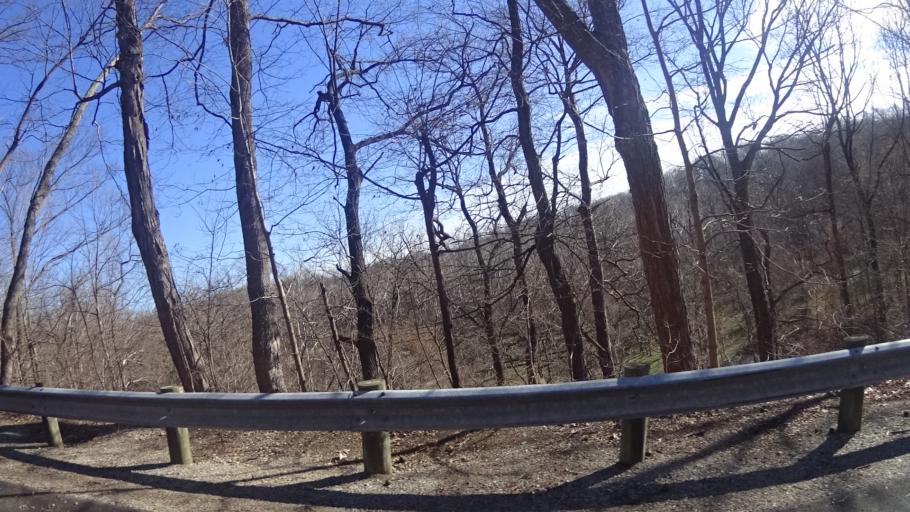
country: US
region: Ohio
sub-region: Lorain County
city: Vermilion
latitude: 41.3506
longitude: -82.3449
